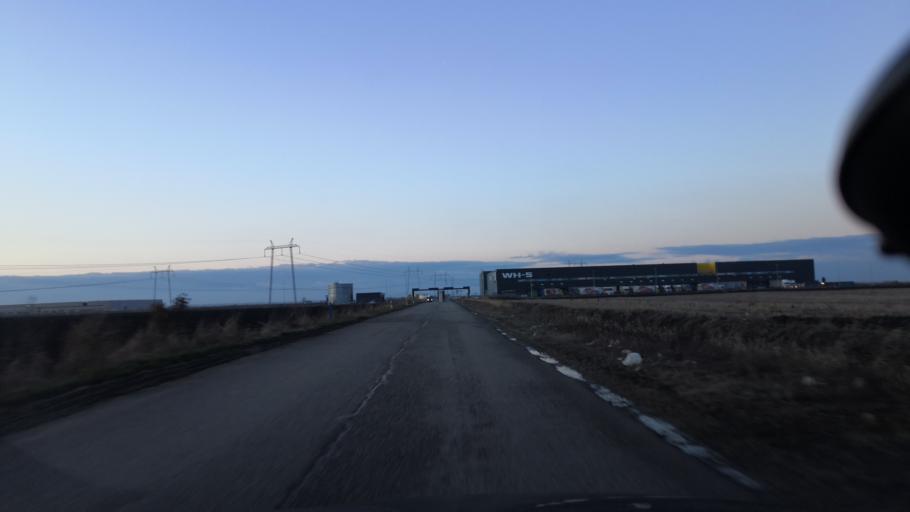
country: RS
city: Simanovci
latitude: 44.8893
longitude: 20.1102
